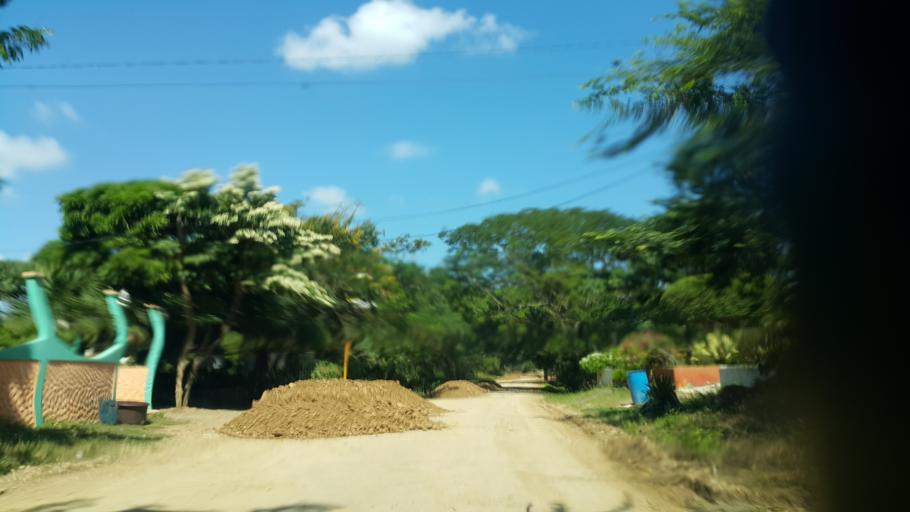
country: NI
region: Rivas
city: San Juan del Sur
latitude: 11.2915
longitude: -85.8902
